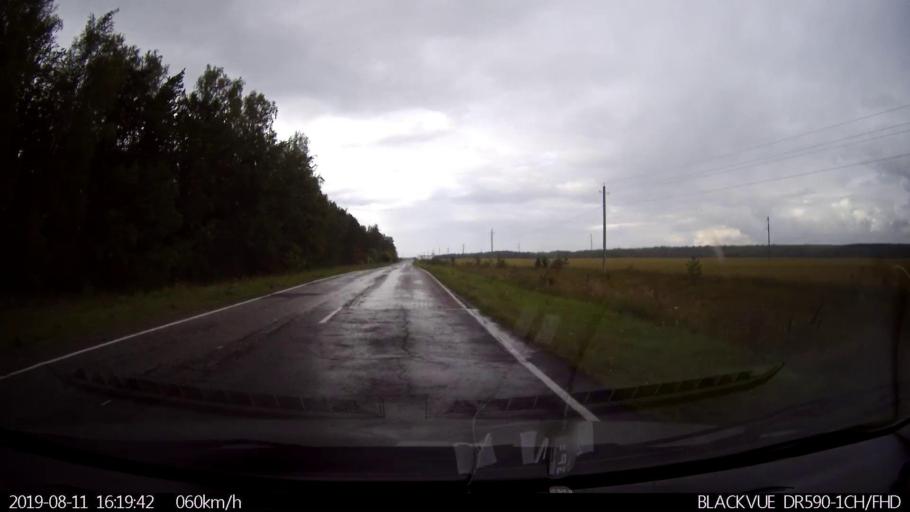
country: RU
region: Ulyanovsk
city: Mayna
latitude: 54.0660
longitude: 47.6061
